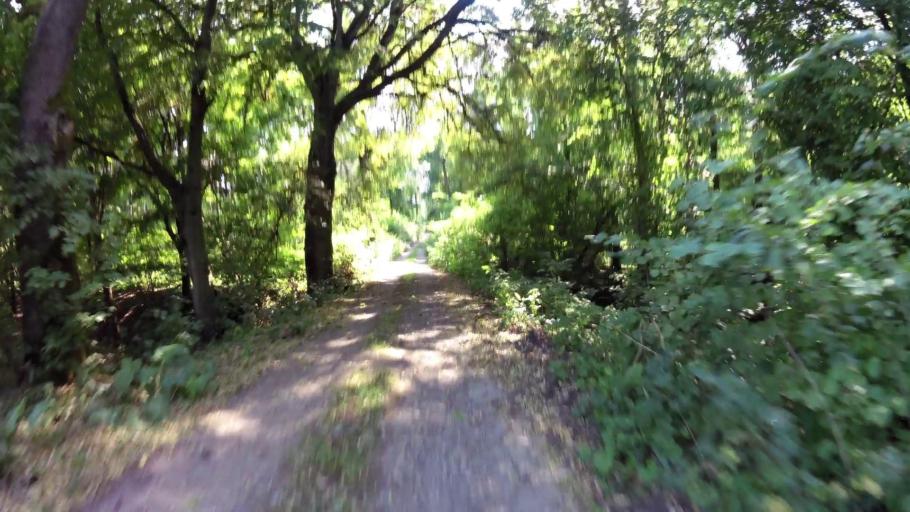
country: PL
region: West Pomeranian Voivodeship
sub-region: Powiat gryfinski
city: Moryn
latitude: 52.8831
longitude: 14.4330
